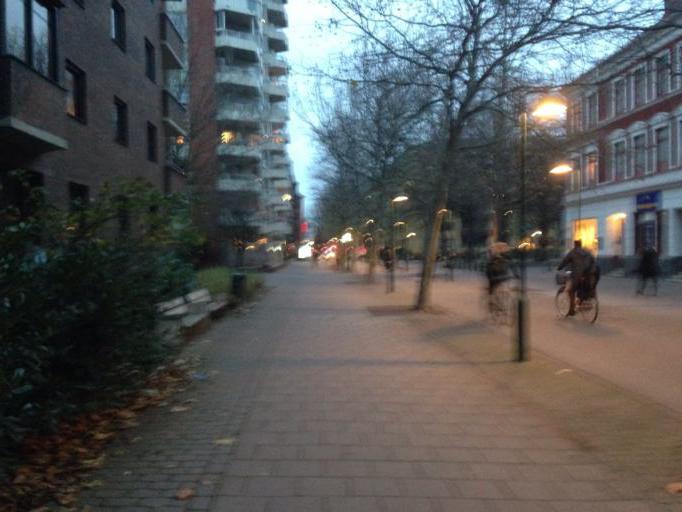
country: SE
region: Skane
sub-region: Malmo
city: Malmoe
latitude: 55.5993
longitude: 13.0056
